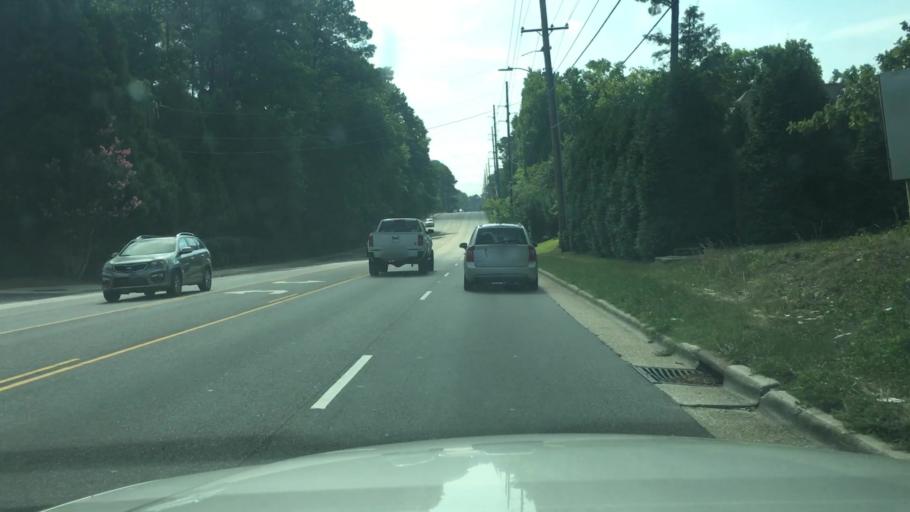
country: US
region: North Carolina
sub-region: Cumberland County
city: Fayetteville
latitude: 35.0667
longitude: -78.9483
